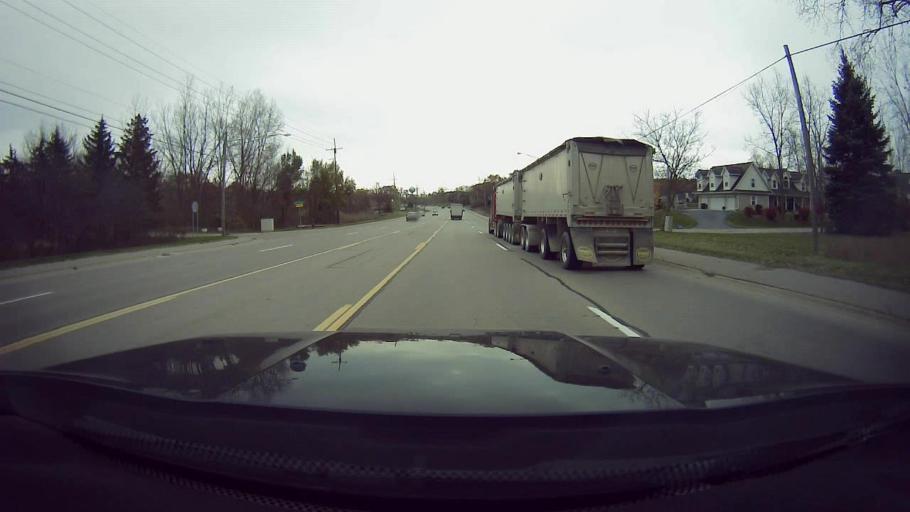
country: US
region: Michigan
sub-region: Oakland County
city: Clarkston
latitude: 42.7320
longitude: -83.4432
